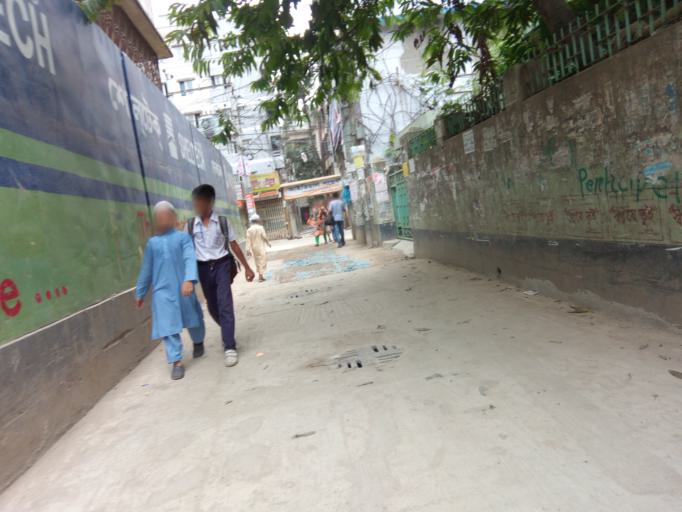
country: BD
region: Dhaka
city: Paltan
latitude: 23.7555
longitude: 90.4114
